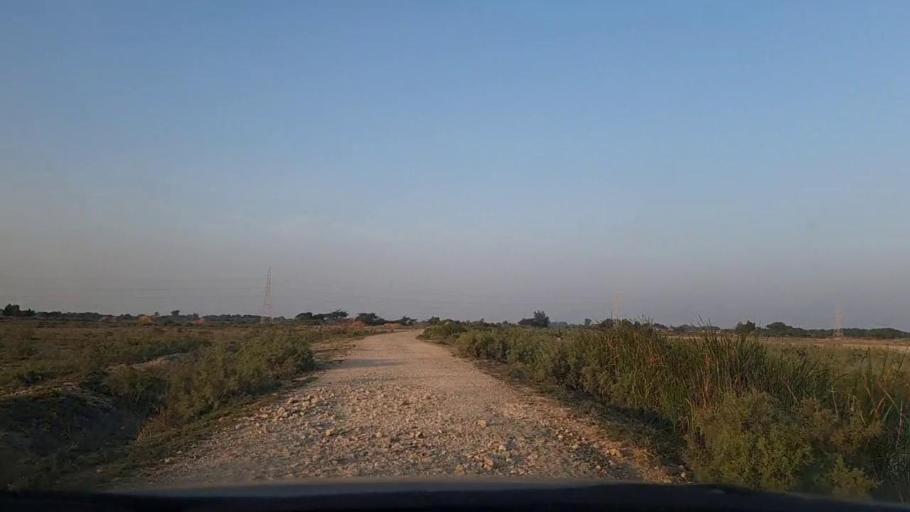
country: PK
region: Sindh
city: Mirpur Sakro
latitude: 24.5584
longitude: 67.6578
